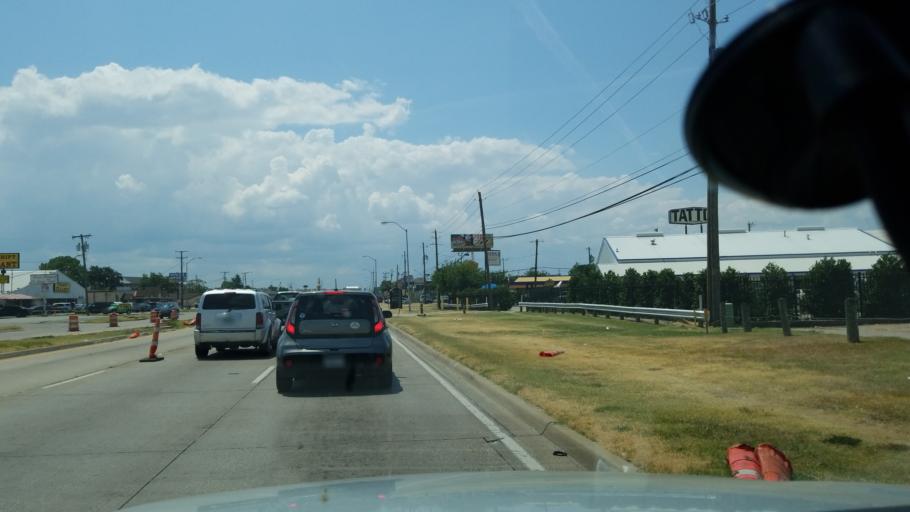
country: US
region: Texas
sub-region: Dallas County
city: Farmers Branch
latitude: 32.8695
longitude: -96.8828
